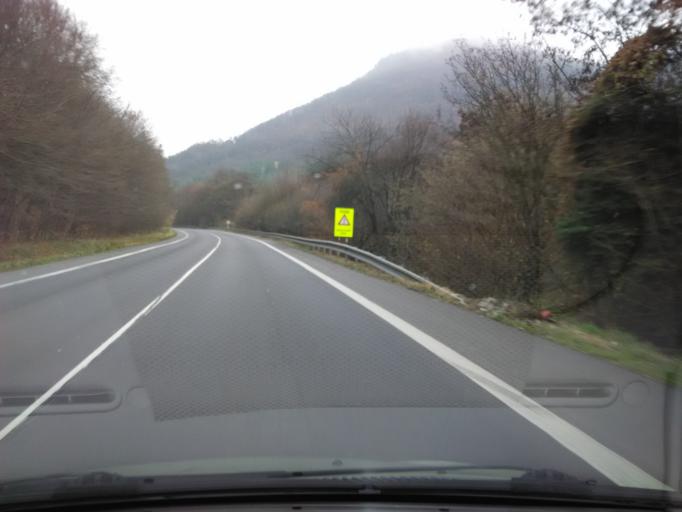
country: SK
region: Banskobystricky
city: Ziar nad Hronom
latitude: 48.5927
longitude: 18.8948
